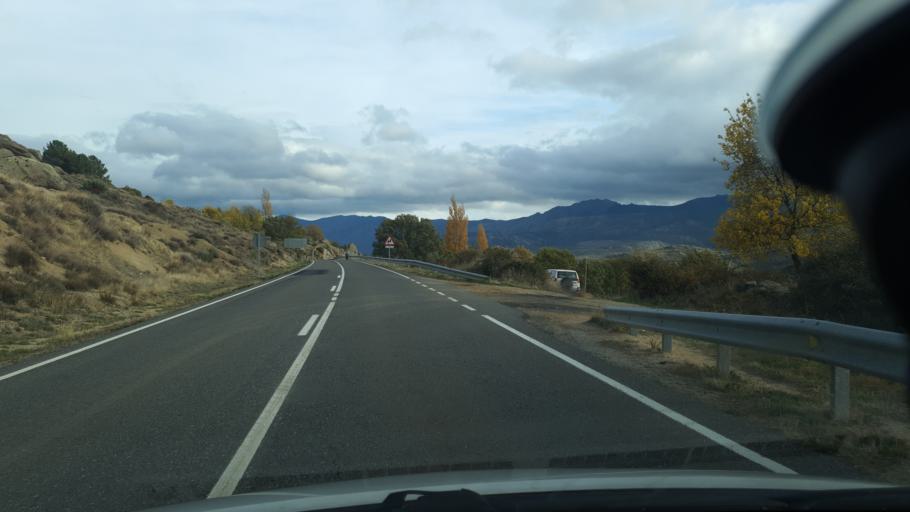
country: ES
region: Castille and Leon
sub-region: Provincia de Avila
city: Navalosa
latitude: 40.3966
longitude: -4.9264
